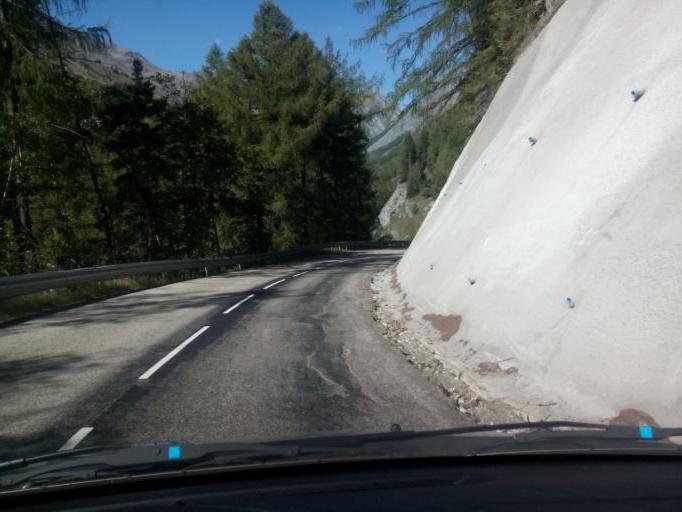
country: FR
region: Rhone-Alpes
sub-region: Departement de l'Isere
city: Mont-de-Lans
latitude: 45.0671
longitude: 6.1564
